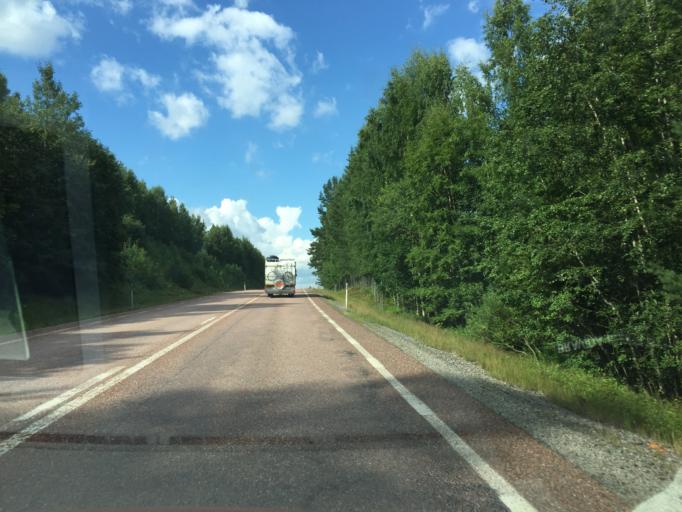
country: SE
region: Gaevleborg
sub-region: Bollnas Kommun
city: Kilafors
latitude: 61.1983
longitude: 16.7618
